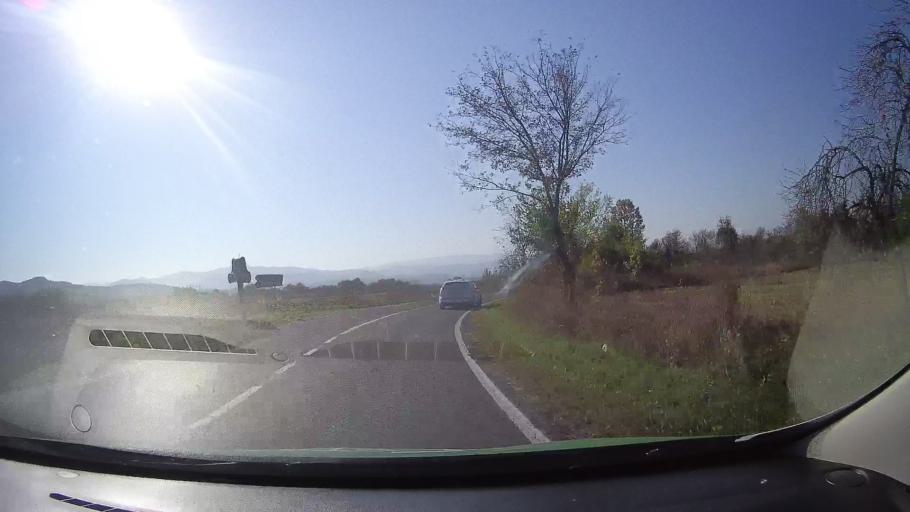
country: RO
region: Timis
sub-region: Comuna Curtea
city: Curtea
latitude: 45.8469
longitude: 22.3137
